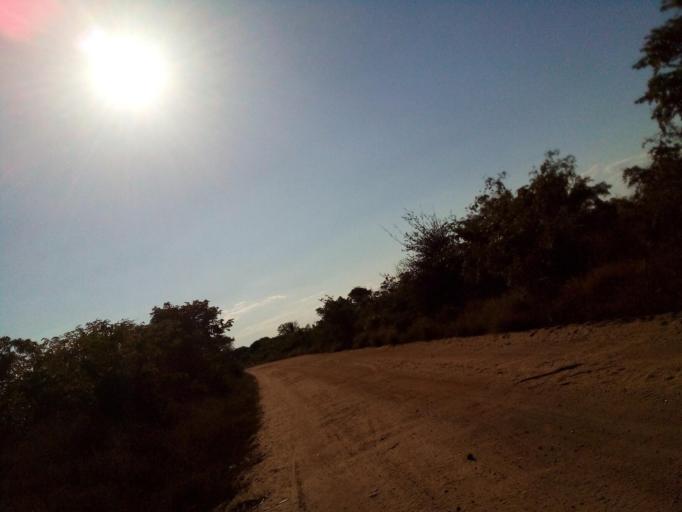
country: MZ
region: Zambezia
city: Quelimane
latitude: -17.4968
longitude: 36.5736
